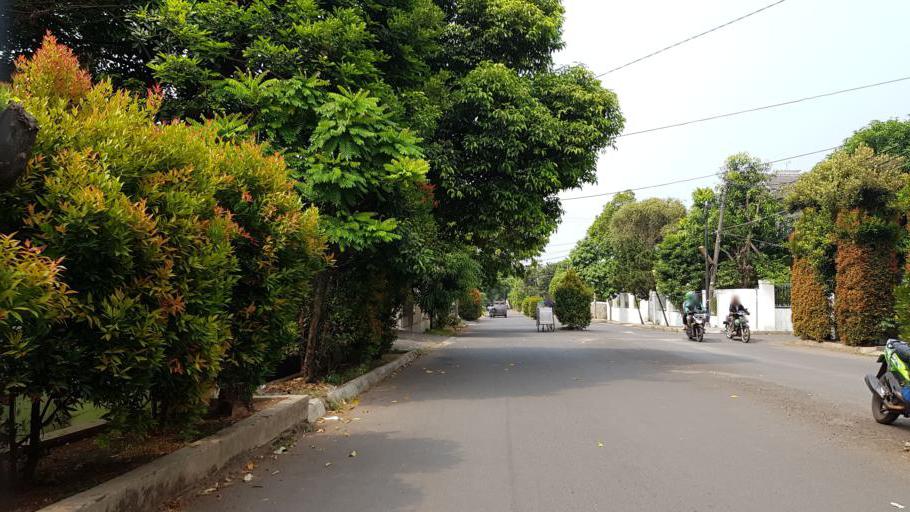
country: ID
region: West Java
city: Pamulang
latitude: -6.3290
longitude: 106.7869
